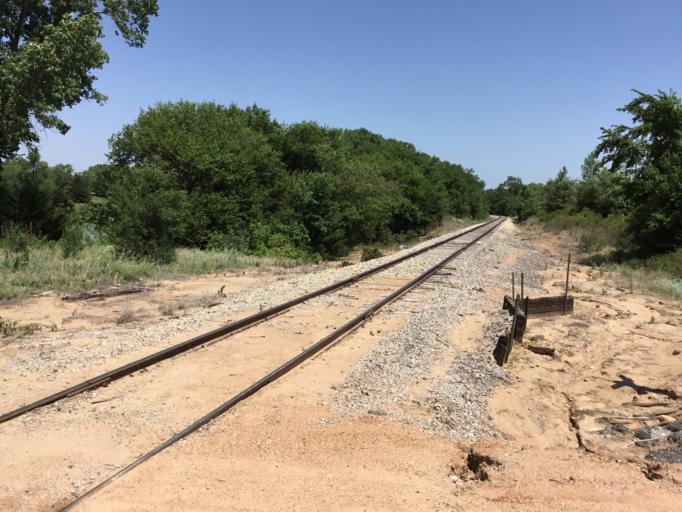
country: US
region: Kansas
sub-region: Kingman County
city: Kingman
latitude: 37.6183
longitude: -98.1380
